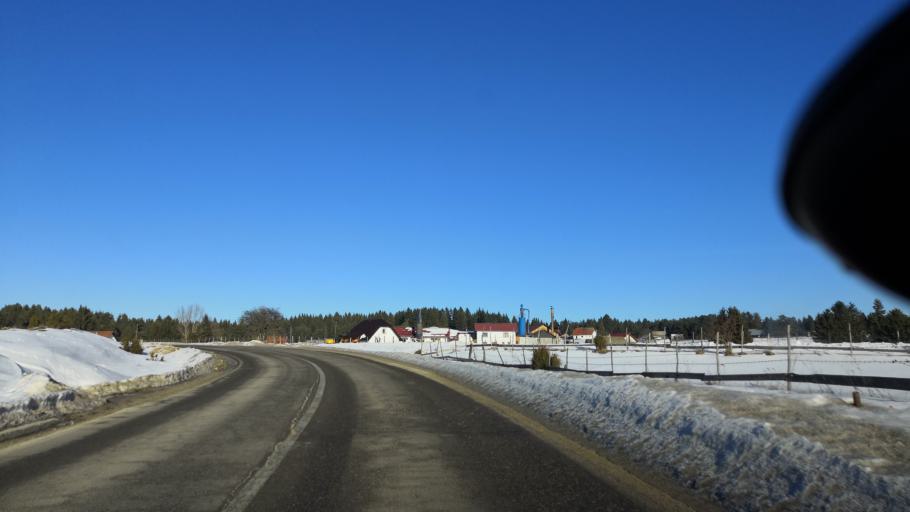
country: BA
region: Republika Srpska
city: Han Pijesak
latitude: 44.0364
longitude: 18.9265
